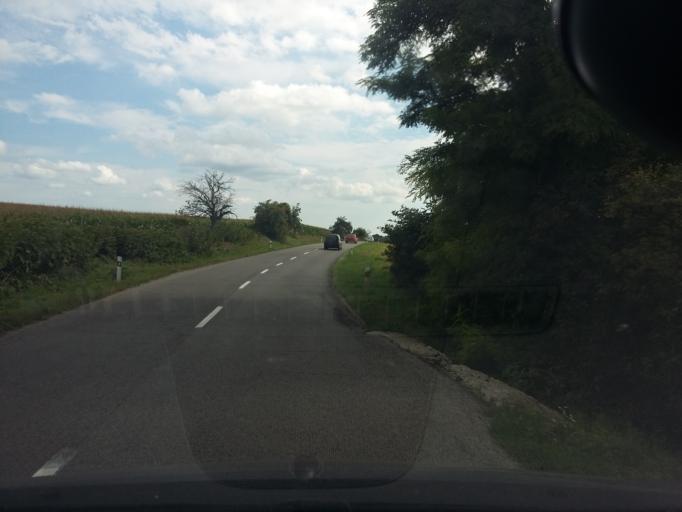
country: SK
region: Trnavsky
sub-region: Okres Skalica
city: Holic
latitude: 48.7506
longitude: 17.1705
